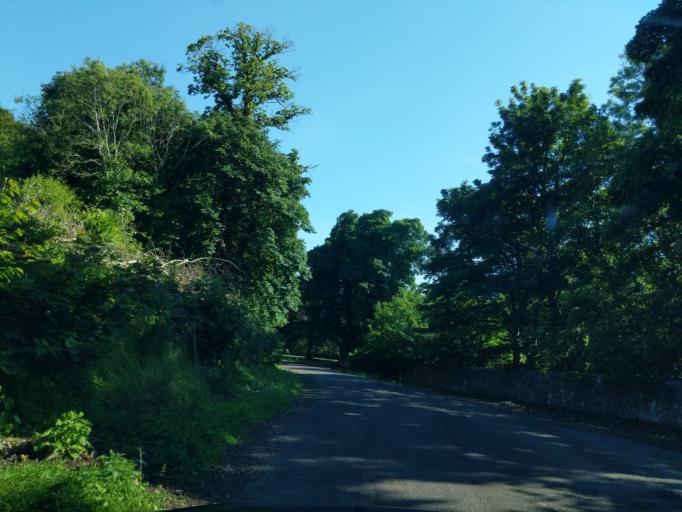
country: GB
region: Scotland
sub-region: Fife
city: Pathhead
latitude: 55.8758
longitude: -2.9722
